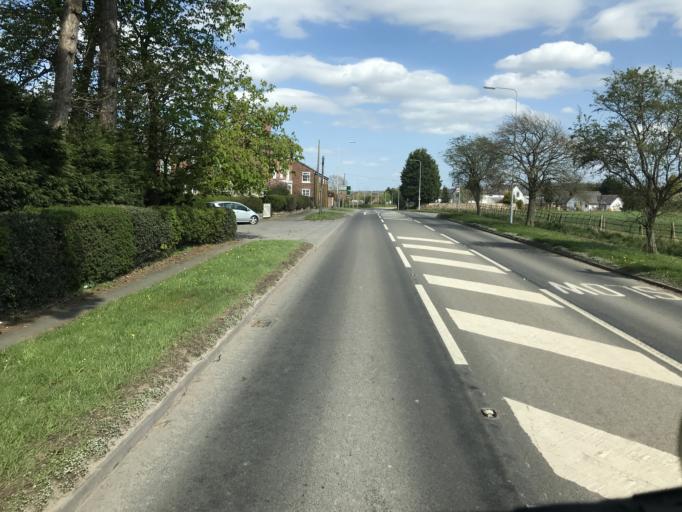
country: GB
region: England
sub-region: Cheshire West and Chester
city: Tarvin
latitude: 53.2026
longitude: -2.7584
